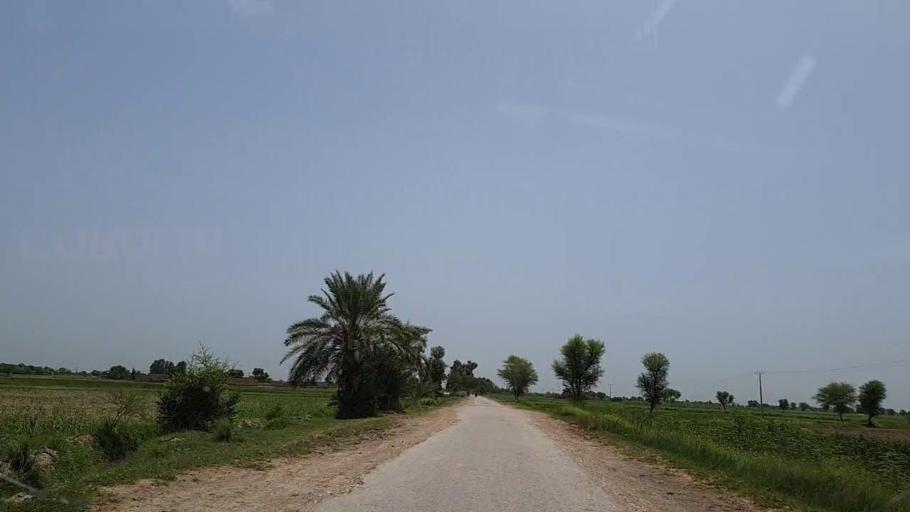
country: PK
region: Sindh
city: Tharu Shah
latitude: 26.9637
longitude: 68.0540
